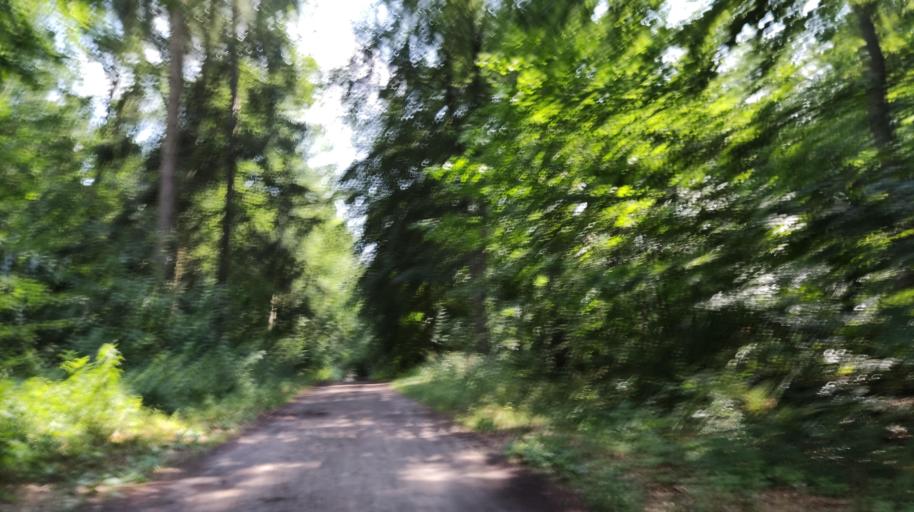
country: DE
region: Lower Saxony
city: Deutsch Evern
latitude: 53.2209
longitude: 10.4238
